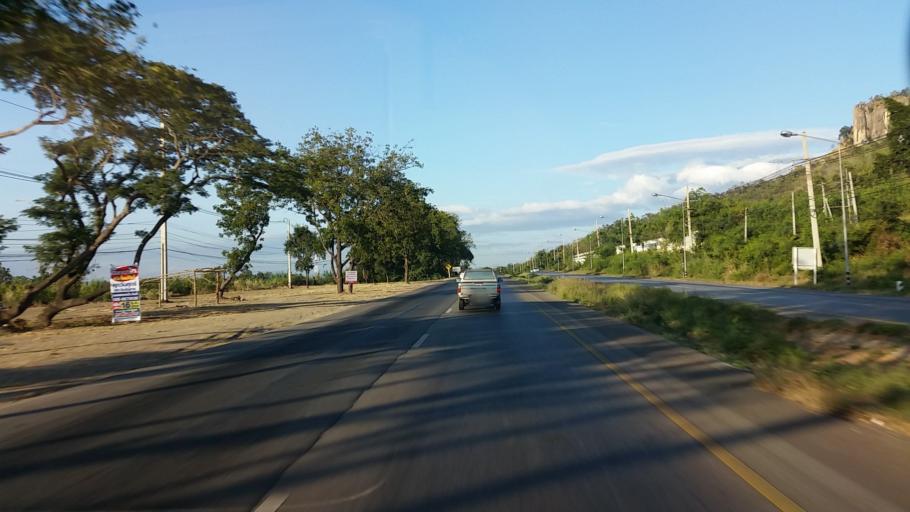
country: TH
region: Lop Buri
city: Chai Badan
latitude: 15.2029
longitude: 101.0923
